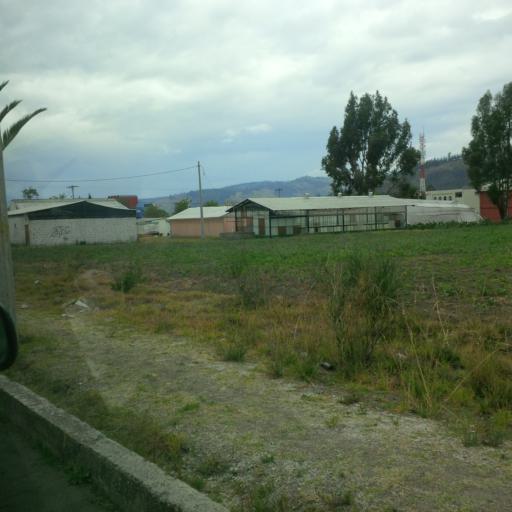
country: EC
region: Chimborazo
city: Riobamba
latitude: -1.6538
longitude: -78.6802
